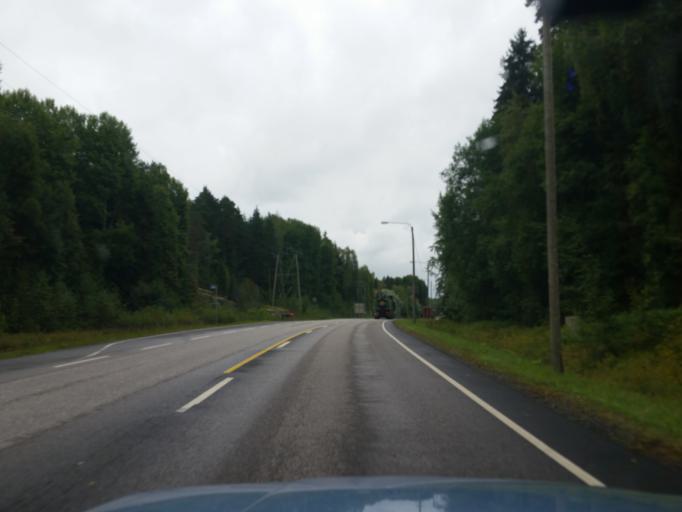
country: FI
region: Uusimaa
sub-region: Helsinki
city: Lohja
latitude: 60.3595
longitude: 24.1747
